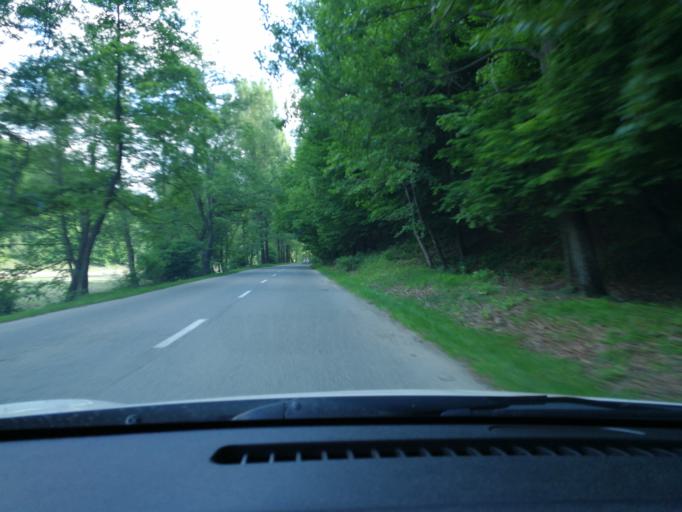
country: RO
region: Prahova
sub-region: Comuna Sotrile
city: Sotrile
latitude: 45.2269
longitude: 25.7314
